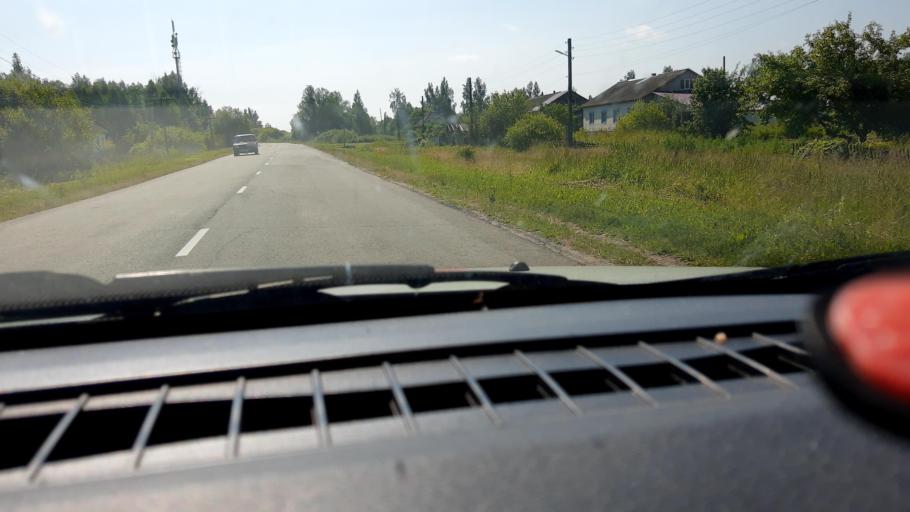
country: RU
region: Nizjnij Novgorod
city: Sharanga
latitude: 57.0466
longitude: 46.5510
